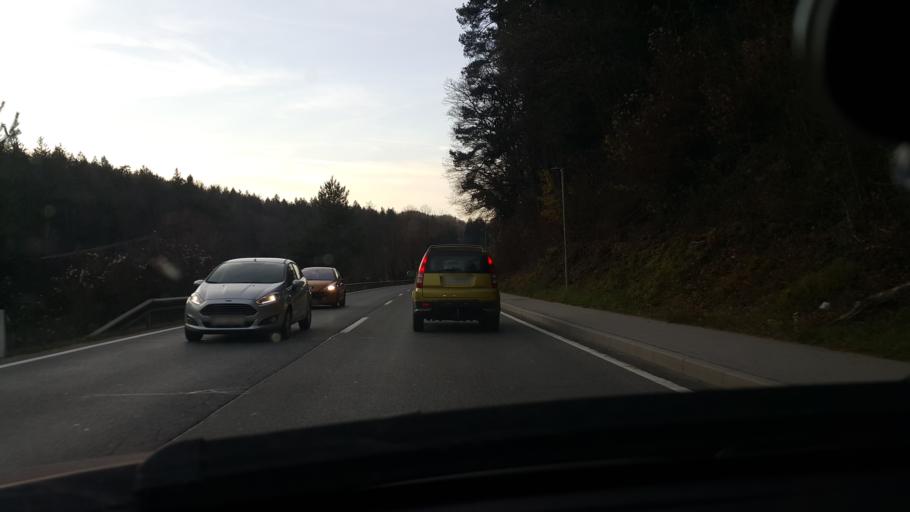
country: SI
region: Velenje
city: Velenje
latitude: 46.3536
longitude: 15.1224
